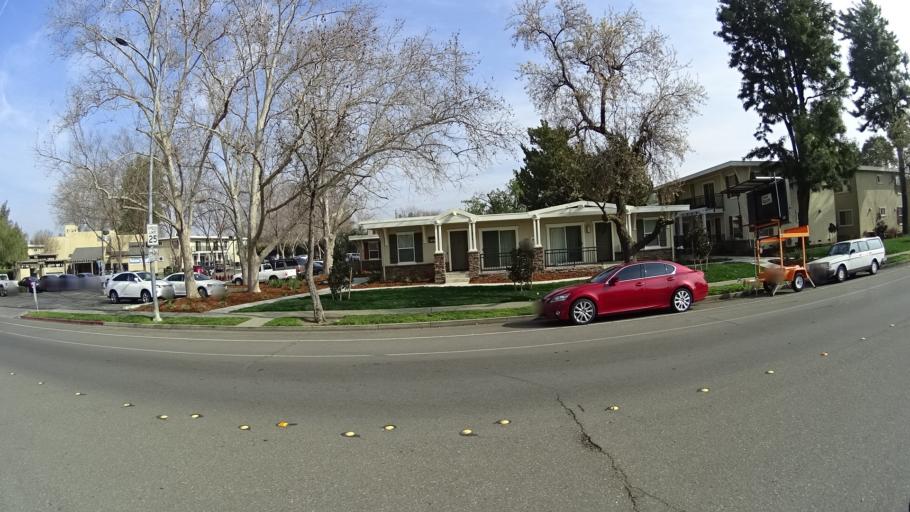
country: US
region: California
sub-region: Yolo County
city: Davis
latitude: 38.5576
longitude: -121.7436
